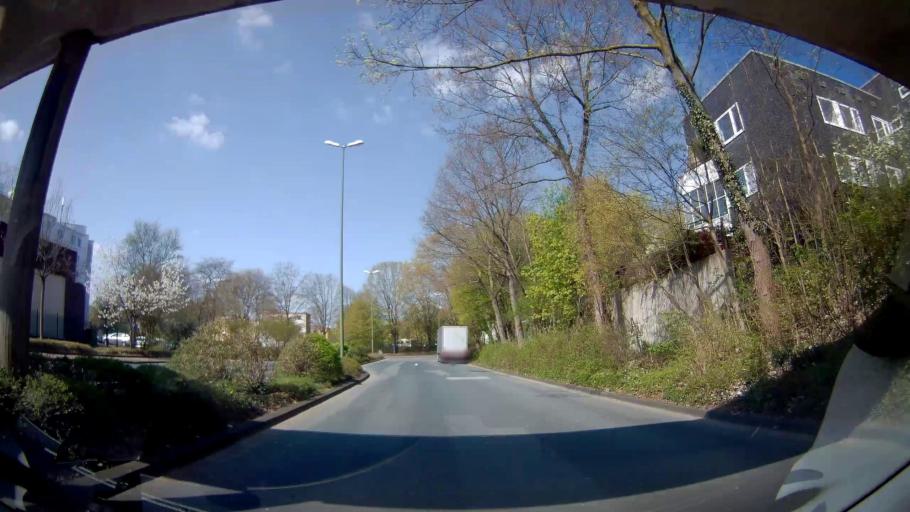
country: DE
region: North Rhine-Westphalia
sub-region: Regierungsbezirk Munster
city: Klein Reken
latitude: 51.7266
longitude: 7.0426
